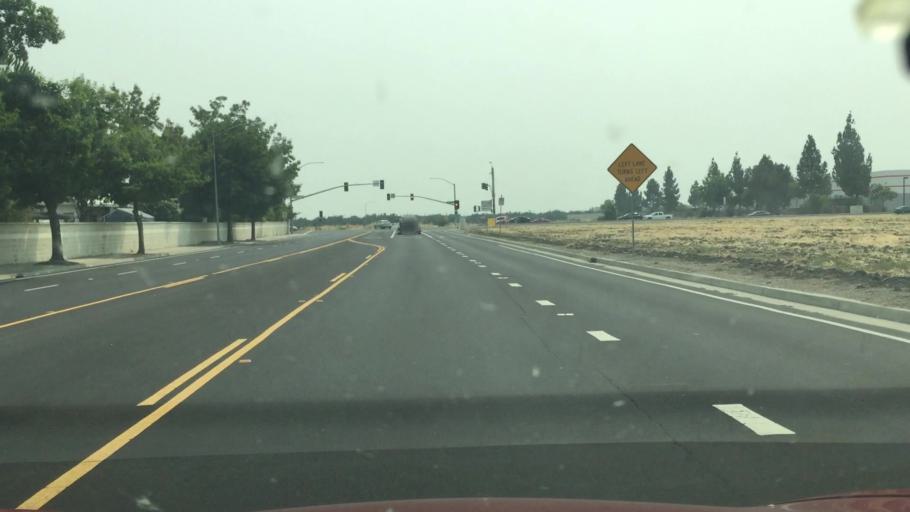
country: US
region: California
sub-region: San Joaquin County
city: Morada
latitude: 38.0226
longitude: -121.2642
